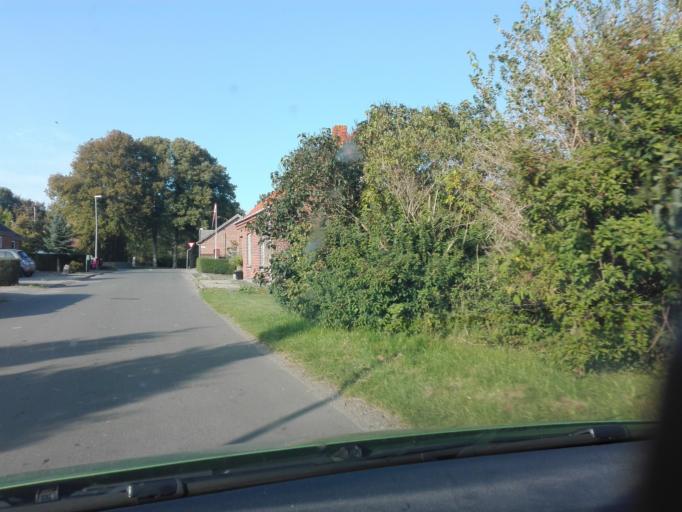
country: DK
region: Central Jutland
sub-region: Odder Kommune
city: Odder
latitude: 55.8893
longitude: 10.1657
